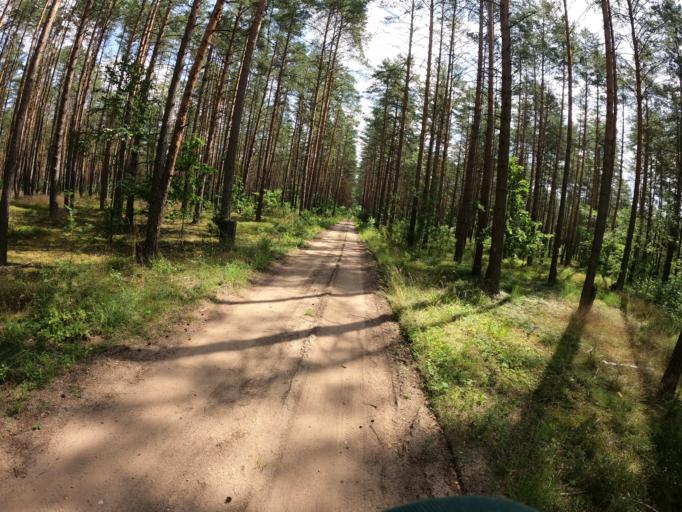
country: LT
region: Alytaus apskritis
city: Druskininkai
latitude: 54.0266
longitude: 23.9405
